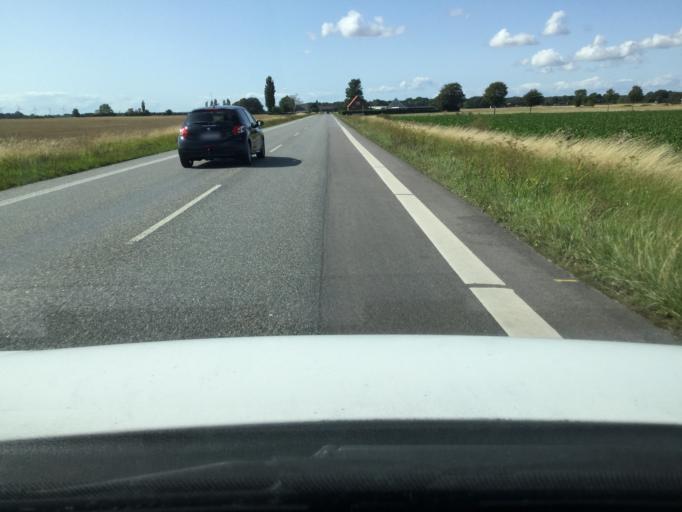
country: DK
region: Zealand
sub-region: Lolland Kommune
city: Rodby
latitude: 54.7510
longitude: 11.3773
